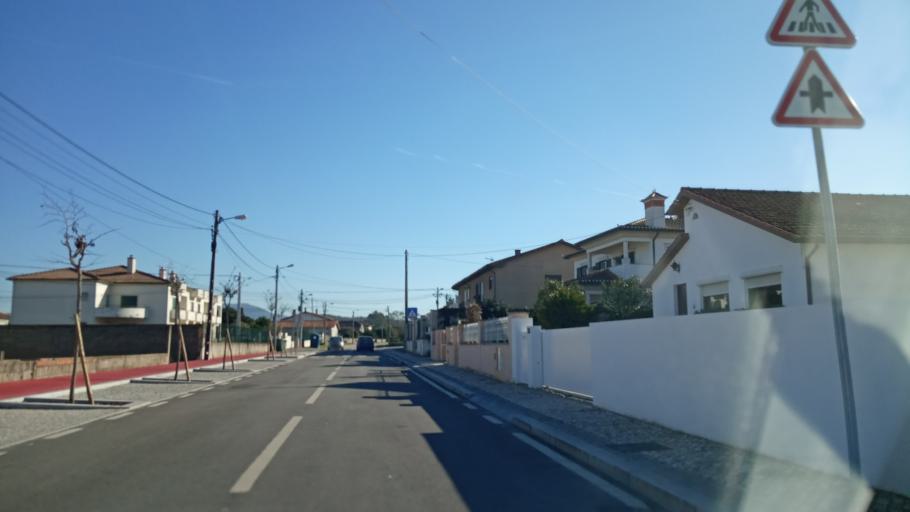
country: PT
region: Aveiro
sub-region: Anadia
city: Anadia
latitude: 40.4313
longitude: -8.4302
